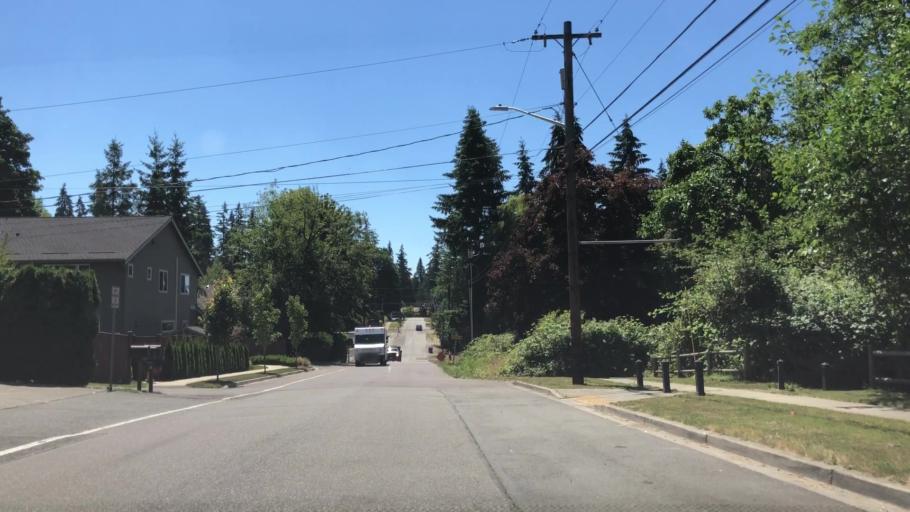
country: US
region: Washington
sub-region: Snohomish County
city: Martha Lake
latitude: 47.8609
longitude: -122.2360
